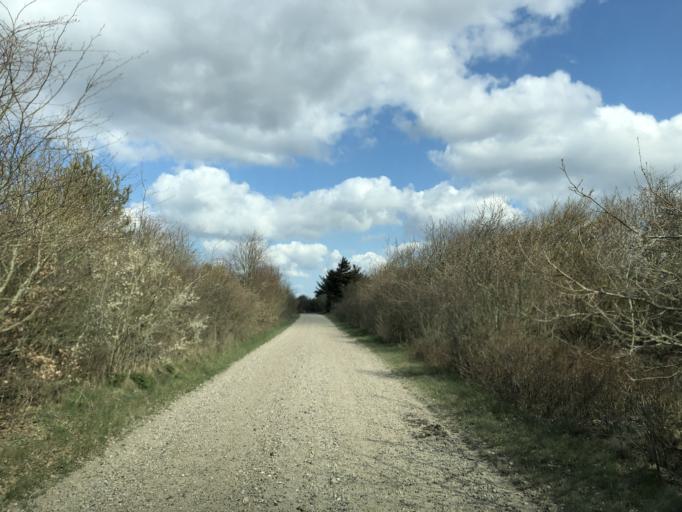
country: DK
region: Central Jutland
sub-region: Holstebro Kommune
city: Ulfborg
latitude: 56.3788
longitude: 8.2095
